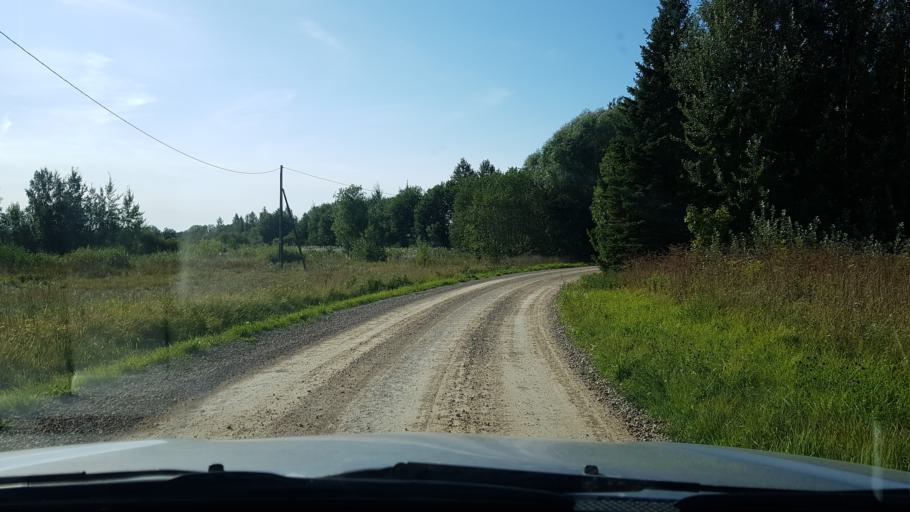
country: EE
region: Ida-Virumaa
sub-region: Narva-Joesuu linn
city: Narva-Joesuu
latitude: 59.4091
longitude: 28.0171
